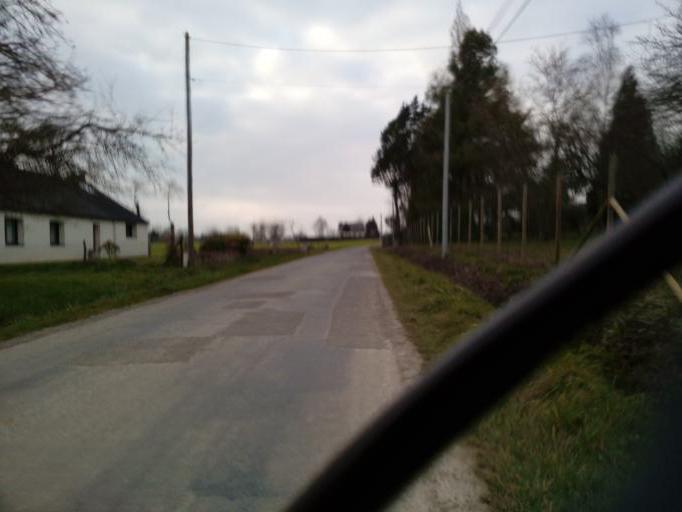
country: FR
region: Brittany
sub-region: Departement d'Ille-et-Vilaine
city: Cintre
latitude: 48.1073
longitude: -1.8949
